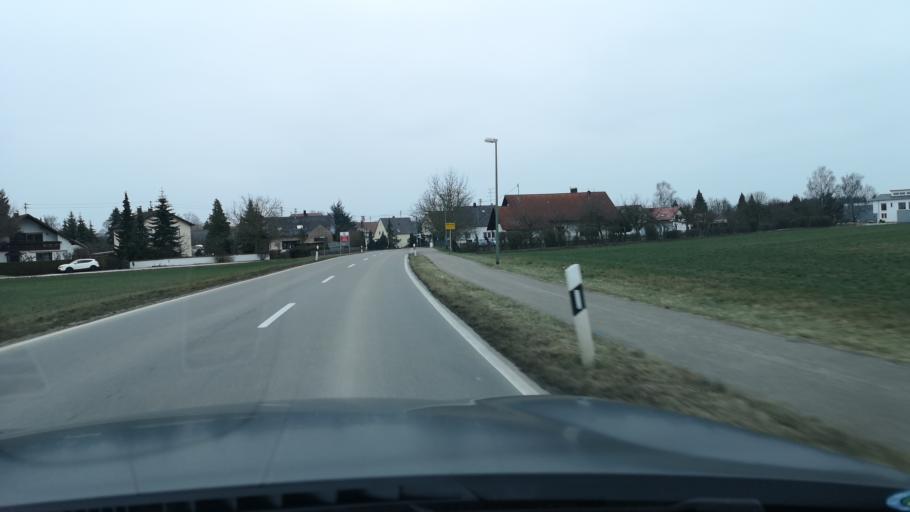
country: DE
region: Bavaria
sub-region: Swabia
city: Nersingen
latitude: 48.4218
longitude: 10.1751
